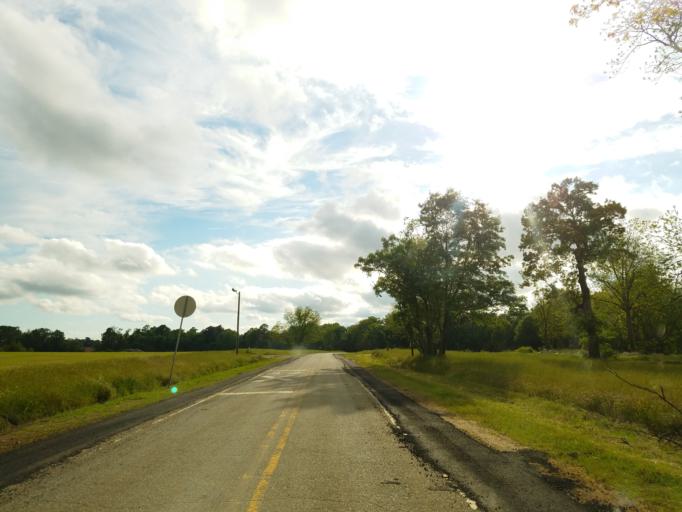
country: US
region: Georgia
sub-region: Dooly County
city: Vienna
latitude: 32.1533
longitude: -83.7732
